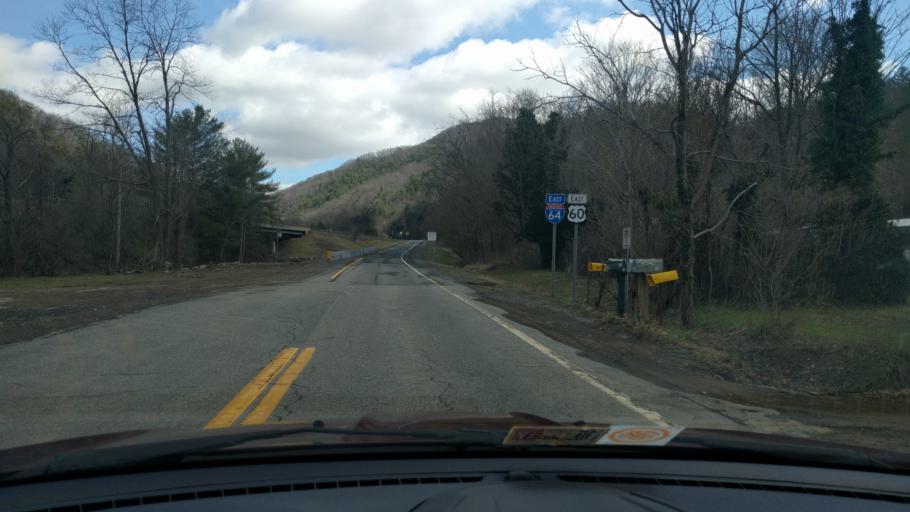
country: US
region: West Virginia
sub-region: Greenbrier County
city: White Sulphur Springs
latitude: 37.7926
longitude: -80.2728
